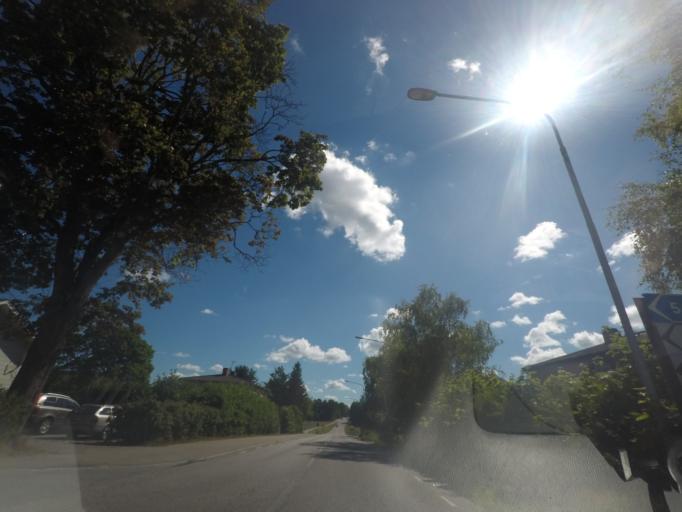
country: SE
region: Stockholm
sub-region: Norrtalje Kommun
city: Nykvarn
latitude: 59.8751
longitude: 18.0482
